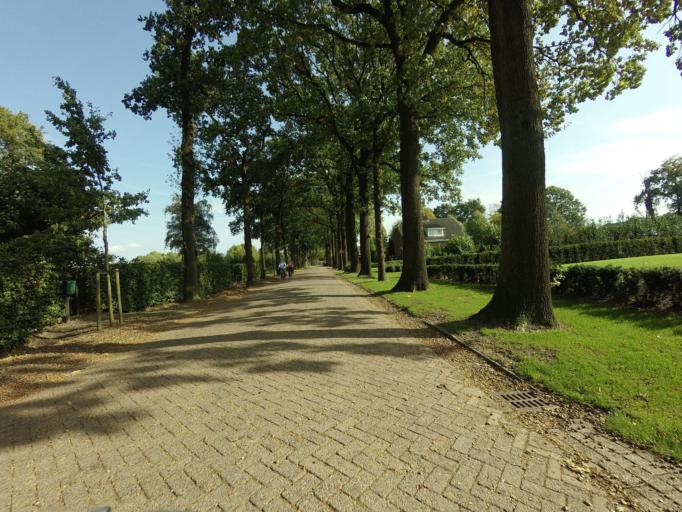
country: NL
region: North Brabant
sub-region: Gemeente Breda
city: Hoge Vucht
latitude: 51.6114
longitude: 4.8124
